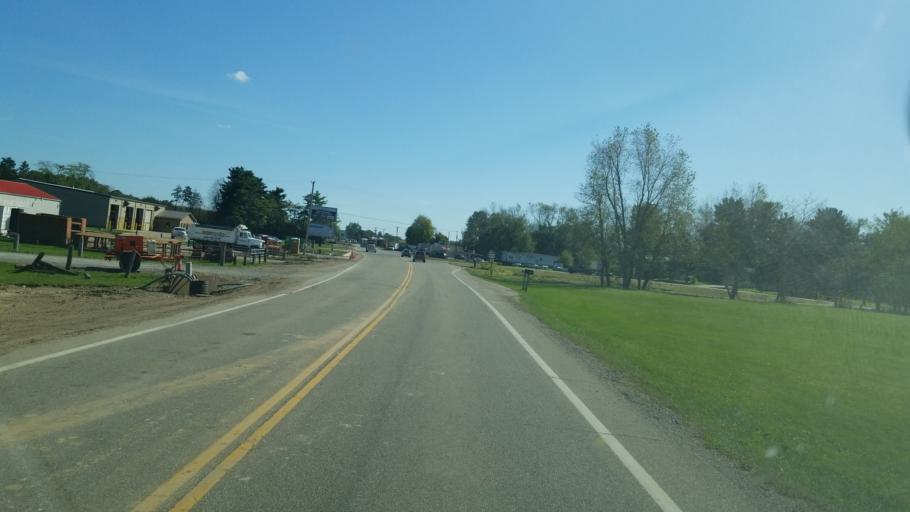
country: US
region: Ohio
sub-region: Tuscarawas County
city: Strasburg
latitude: 40.6270
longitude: -81.5473
